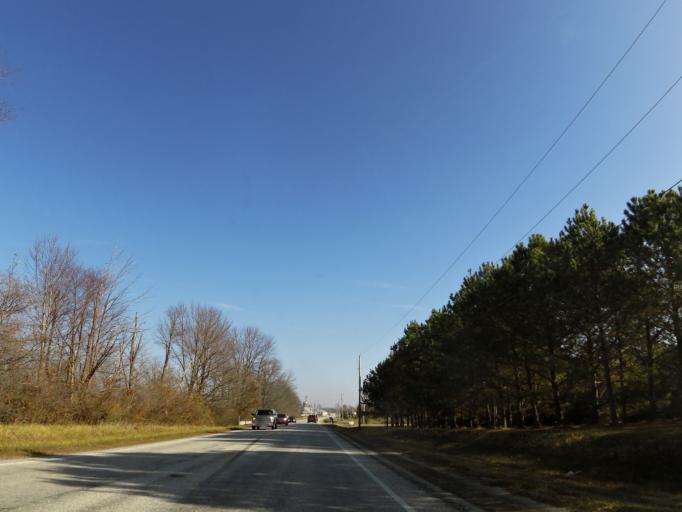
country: US
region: Indiana
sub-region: Shelby County
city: Shelbyville
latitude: 39.5515
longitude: -85.6770
